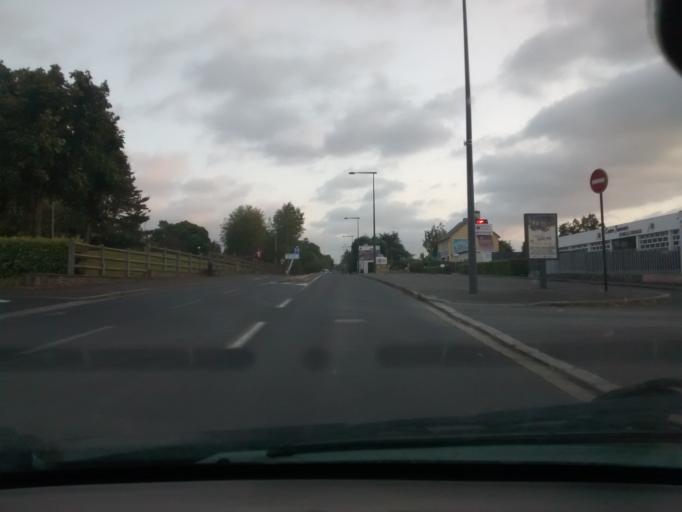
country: FR
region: Lower Normandy
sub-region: Departement de la Manche
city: Agneaux
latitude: 49.1077
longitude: -1.1075
